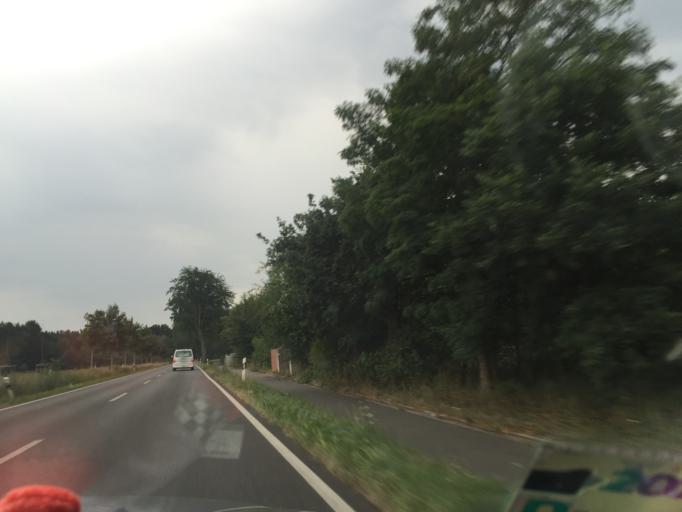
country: DE
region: Brandenburg
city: Zehdenick
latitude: 52.9739
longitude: 13.3546
